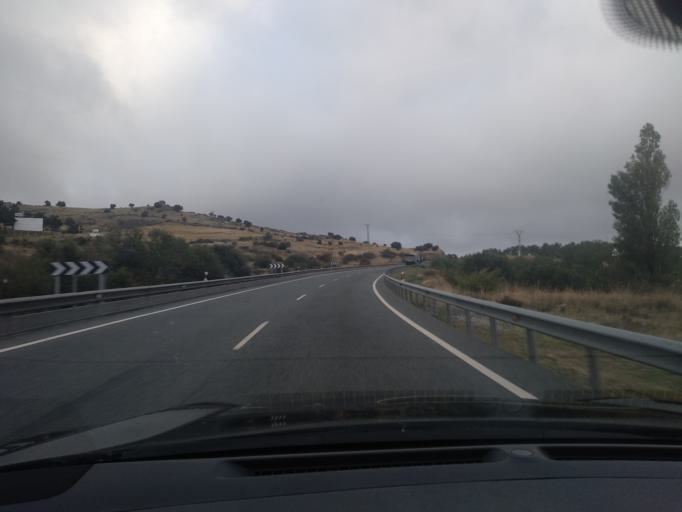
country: ES
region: Castille and Leon
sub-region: Provincia de Segovia
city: Otero de Herreros
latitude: 40.7995
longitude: -4.2112
